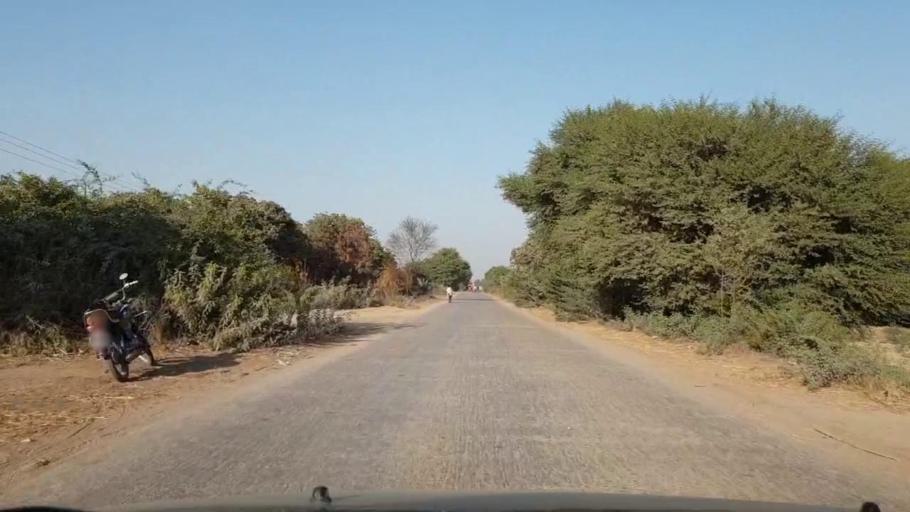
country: PK
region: Sindh
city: Chambar
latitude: 25.2193
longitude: 68.7804
